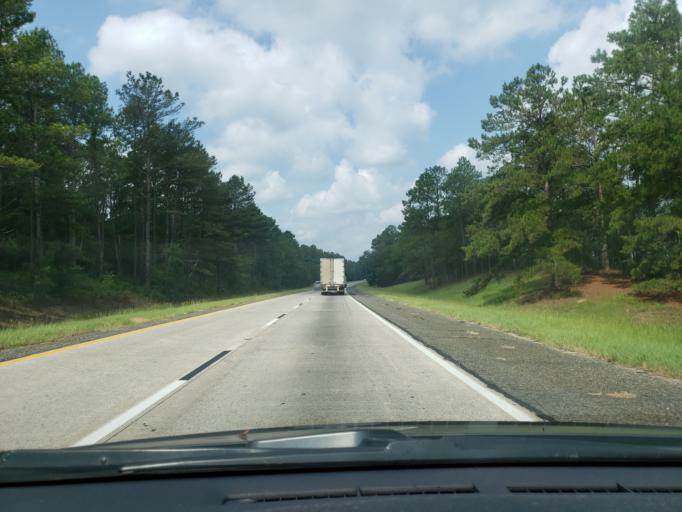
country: US
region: Georgia
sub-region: Treutlen County
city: Soperton
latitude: 32.4268
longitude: -82.5408
